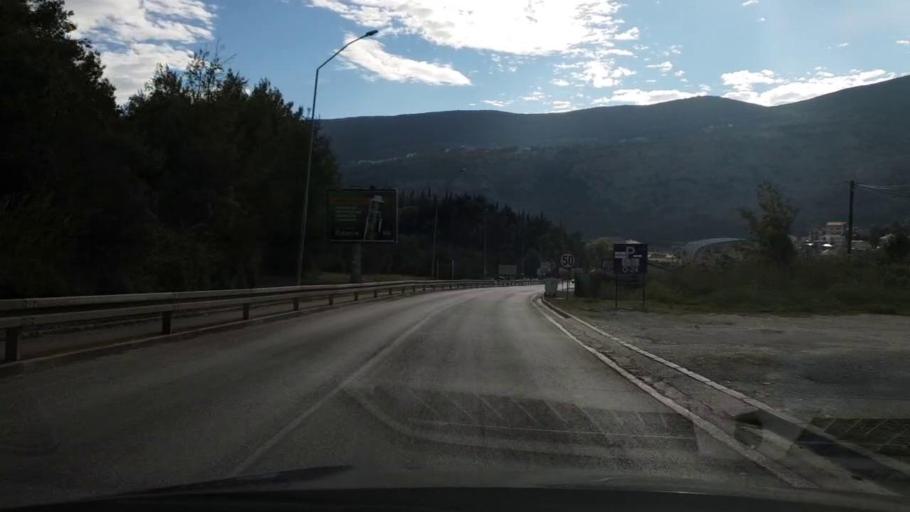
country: ME
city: Igalo
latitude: 42.4600
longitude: 18.5081
